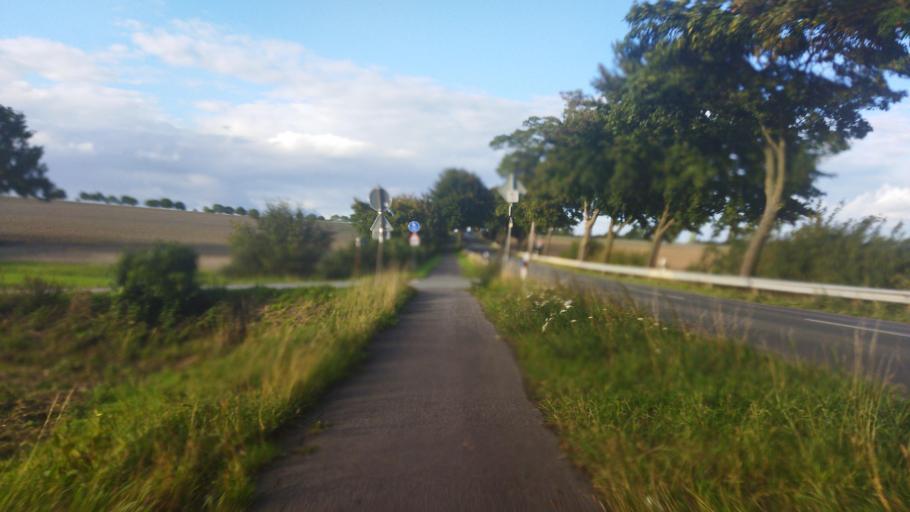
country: DE
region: North Rhine-Westphalia
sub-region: Regierungsbezirk Munster
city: Billerbeck
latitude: 51.9469
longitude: 7.2632
